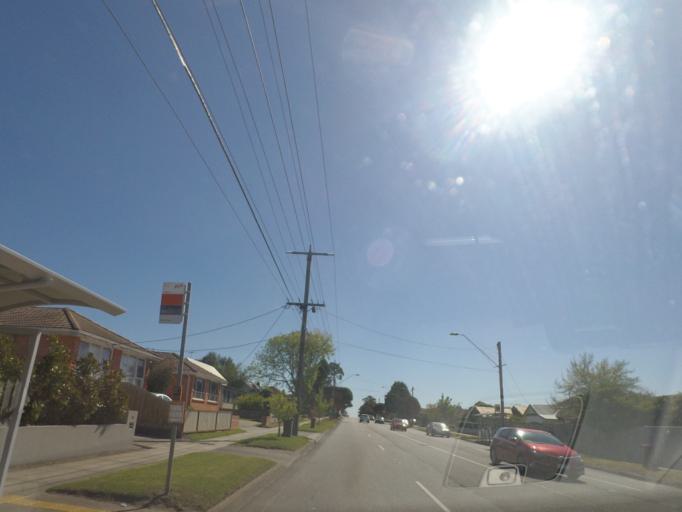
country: AU
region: Victoria
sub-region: Greater Dandenong
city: Noble Park
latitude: -37.9637
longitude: 145.1626
